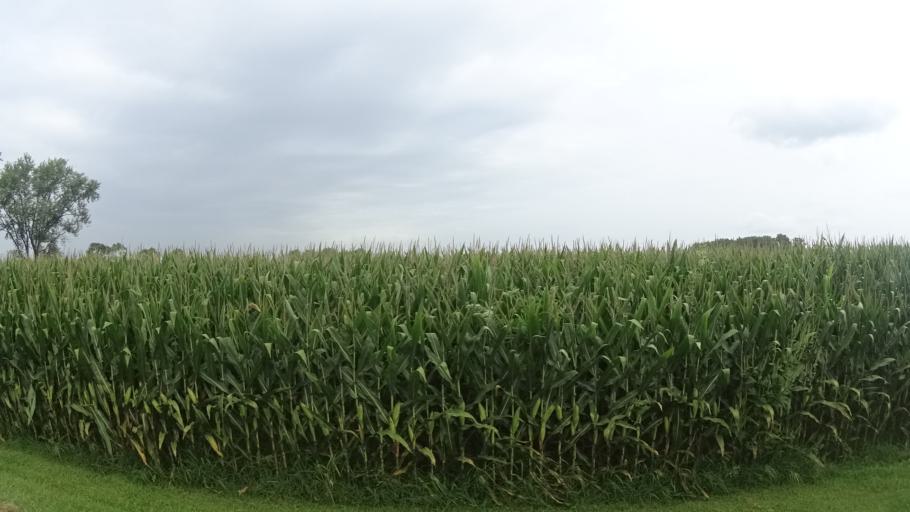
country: US
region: Indiana
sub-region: Madison County
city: Ingalls
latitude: 40.0024
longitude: -85.8415
